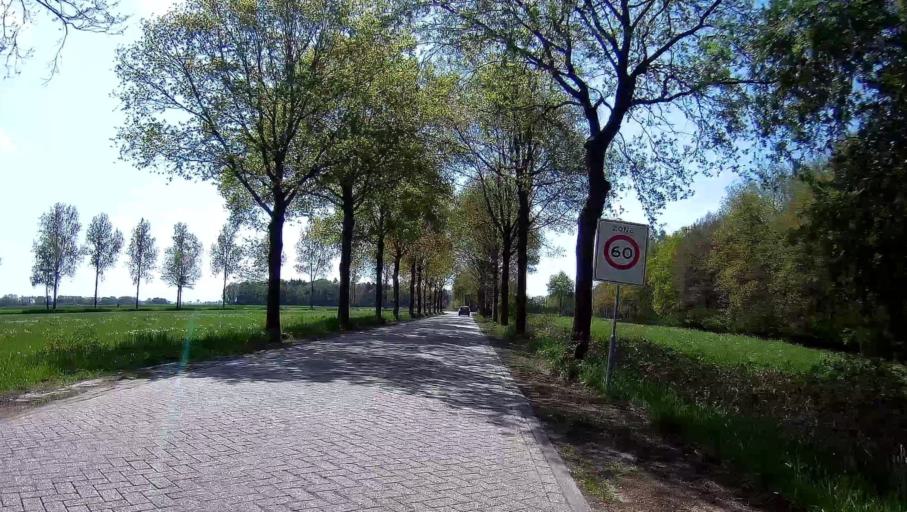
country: NL
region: Drenthe
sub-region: Gemeente Borger-Odoorn
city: Borger
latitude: 52.9624
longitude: 6.8235
